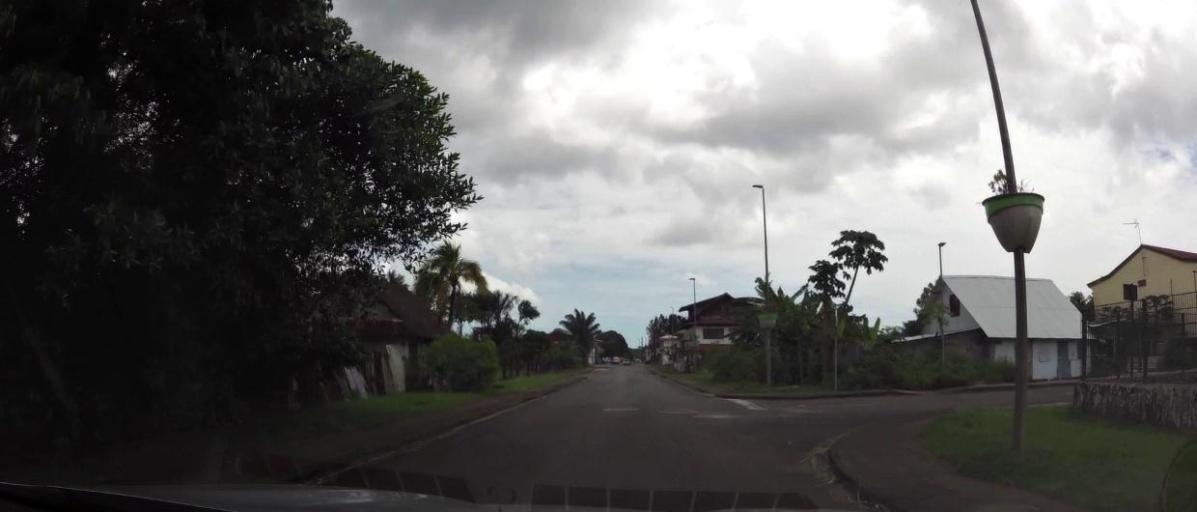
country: GF
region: Guyane
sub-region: Guyane
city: Sinnamary
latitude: 5.3747
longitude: -52.9584
